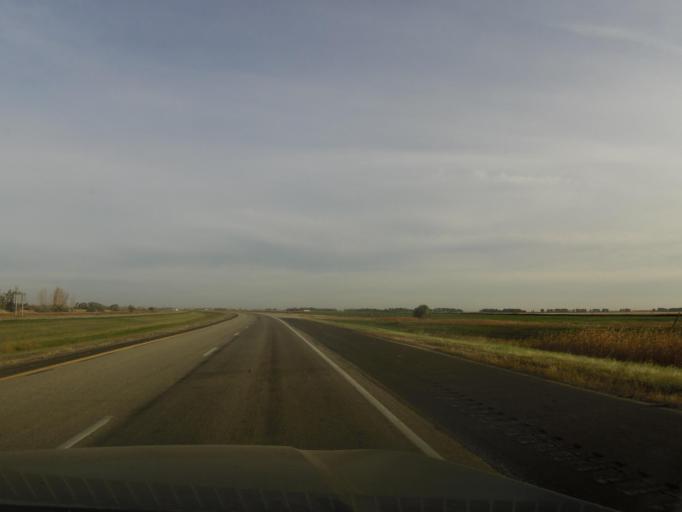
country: US
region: Minnesota
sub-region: Kittson County
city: Hallock
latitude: 48.6598
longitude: -97.1818
